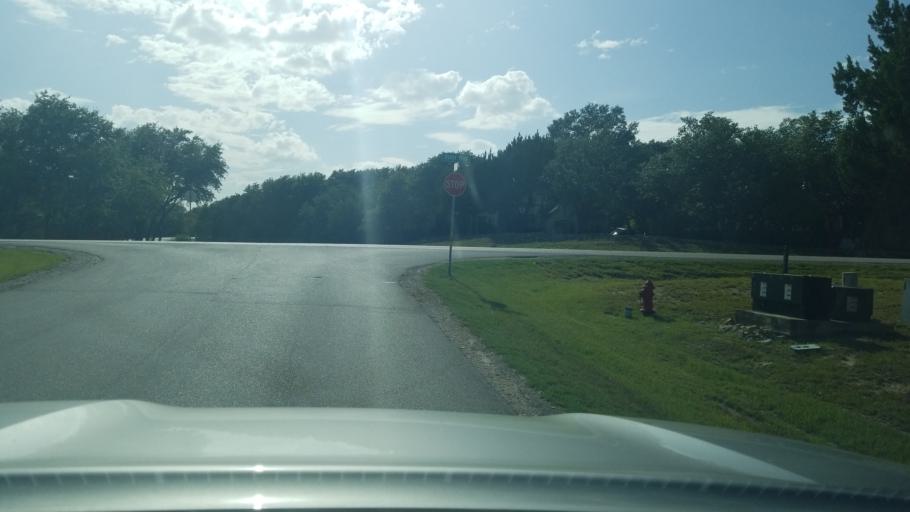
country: US
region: Texas
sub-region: Comal County
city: Bulverde
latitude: 29.8053
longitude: -98.4093
